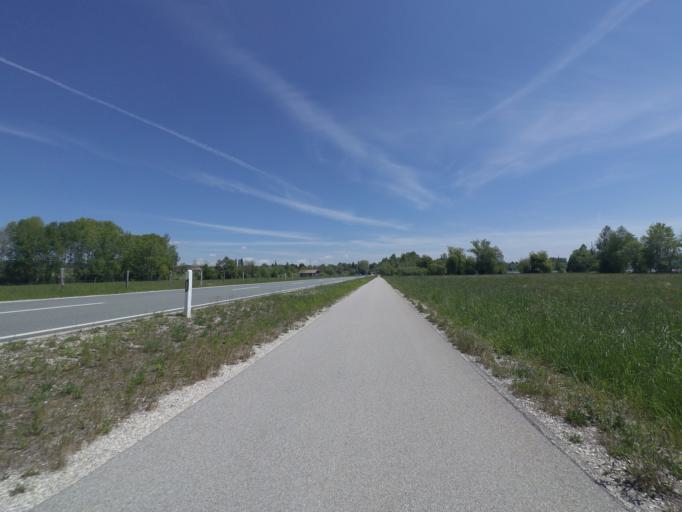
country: DE
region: Bavaria
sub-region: Upper Bavaria
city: Taching am See
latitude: 47.9542
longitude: 12.7430
